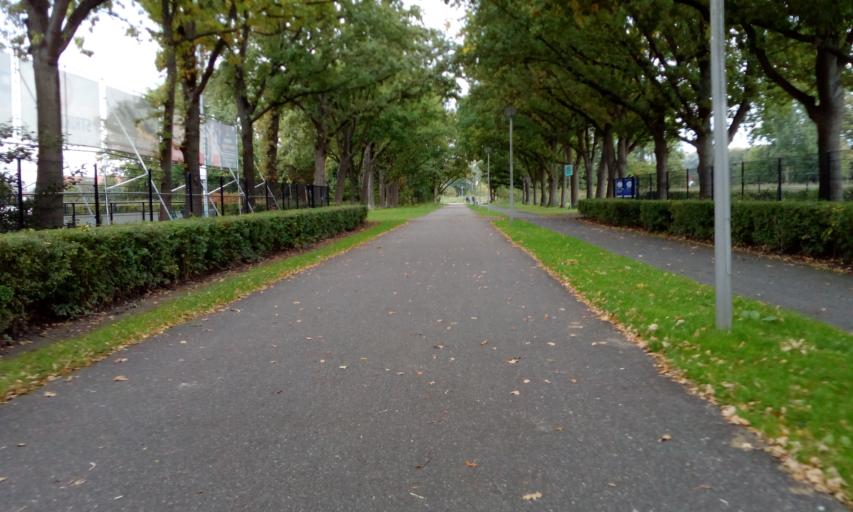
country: NL
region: South Holland
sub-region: Gemeente Rotterdam
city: Delfshaven
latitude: 51.8790
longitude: 4.4750
